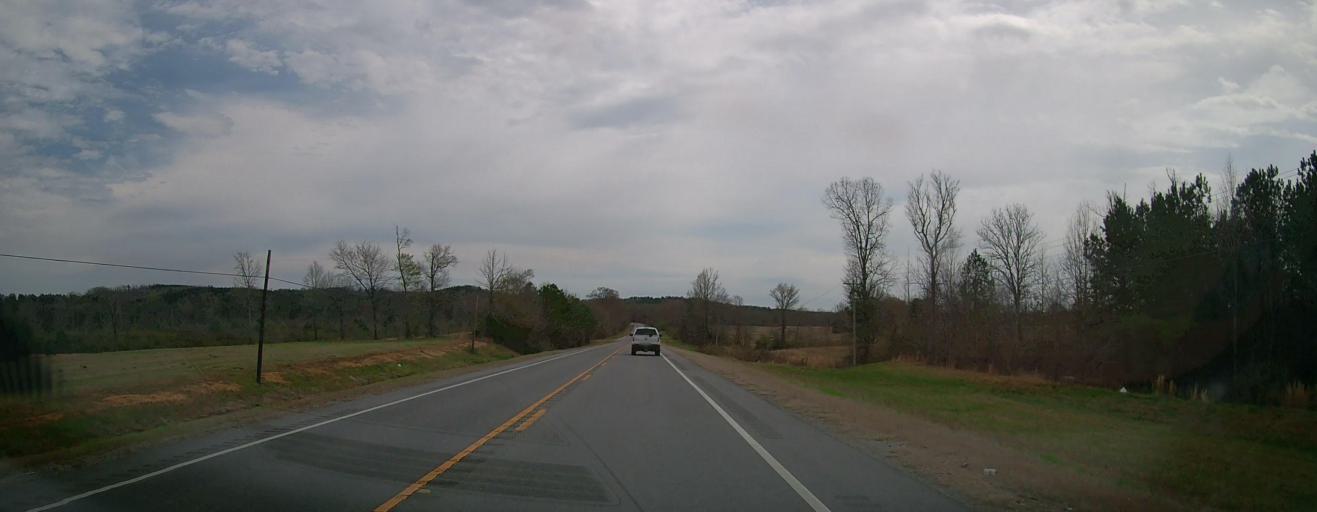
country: US
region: Alabama
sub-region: Marion County
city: Guin
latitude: 34.0050
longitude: -87.9330
